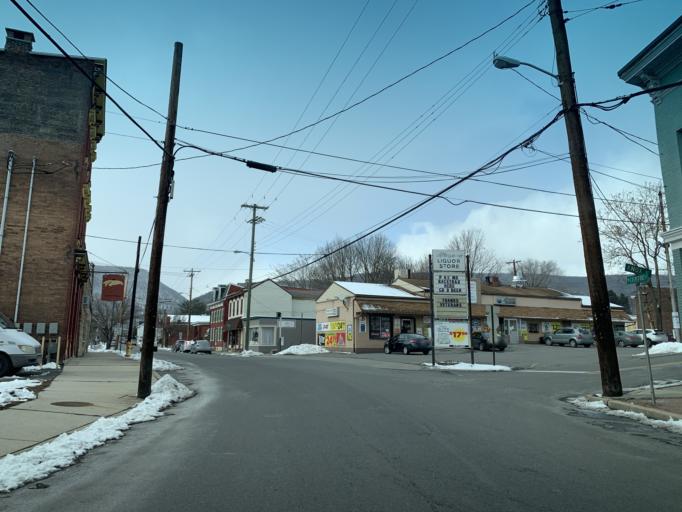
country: US
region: Maryland
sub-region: Allegany County
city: Cumberland
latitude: 39.6562
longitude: -78.7659
